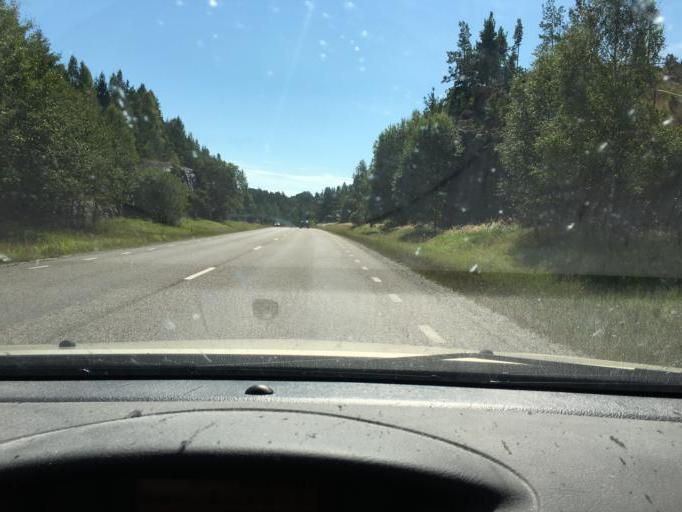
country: SE
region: Stockholm
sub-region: Varmdo Kommun
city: Gustavsberg
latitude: 59.2930
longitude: 18.3929
